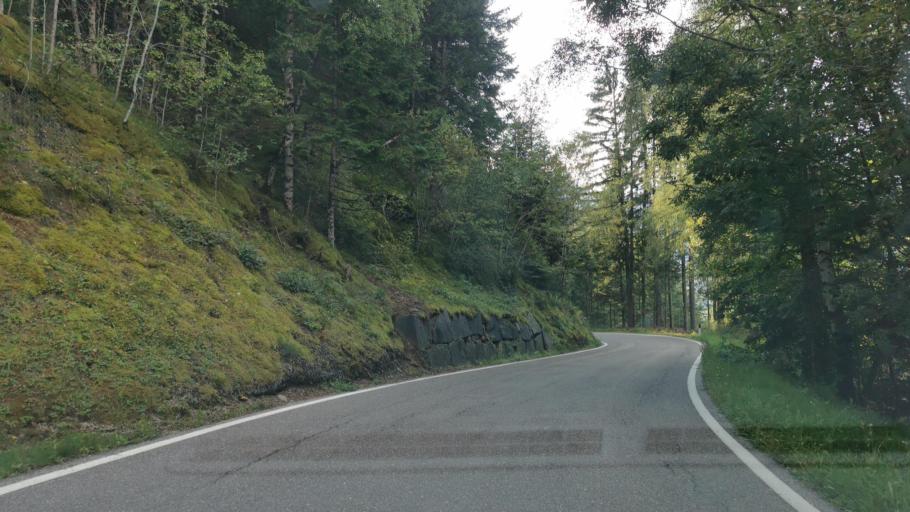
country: IT
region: Trentino-Alto Adige
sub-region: Provincia di Trento
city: Fierozzo
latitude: 46.1059
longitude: 11.3191
